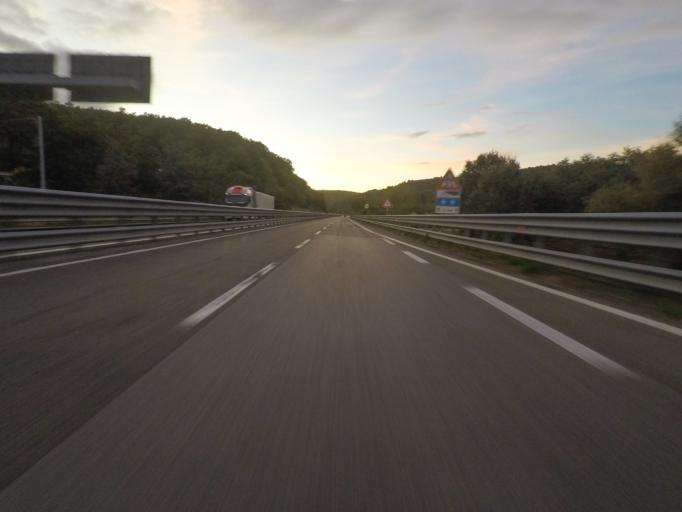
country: IT
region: Tuscany
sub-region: Province of Arezzo
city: Lucignano
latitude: 43.2543
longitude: 11.7070
